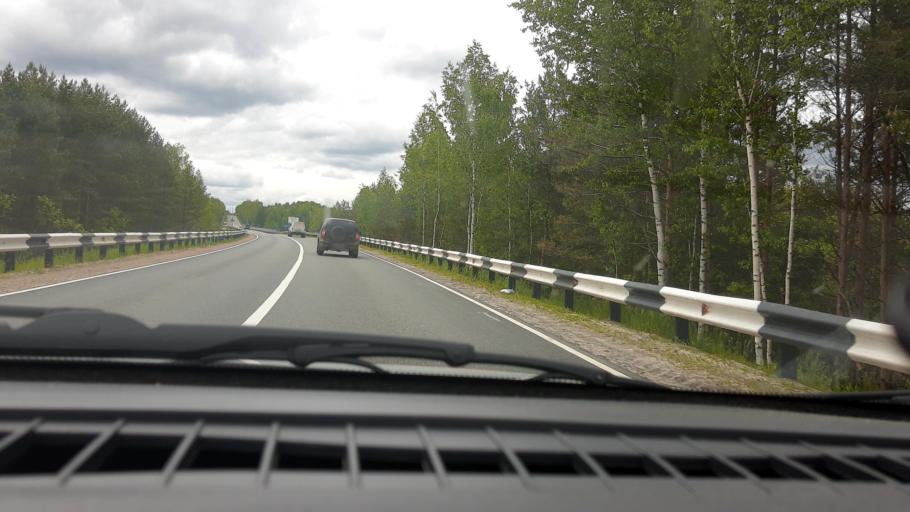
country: RU
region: Nizjnij Novgorod
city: Krasnyye Baki
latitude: 57.1114
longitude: 45.1954
